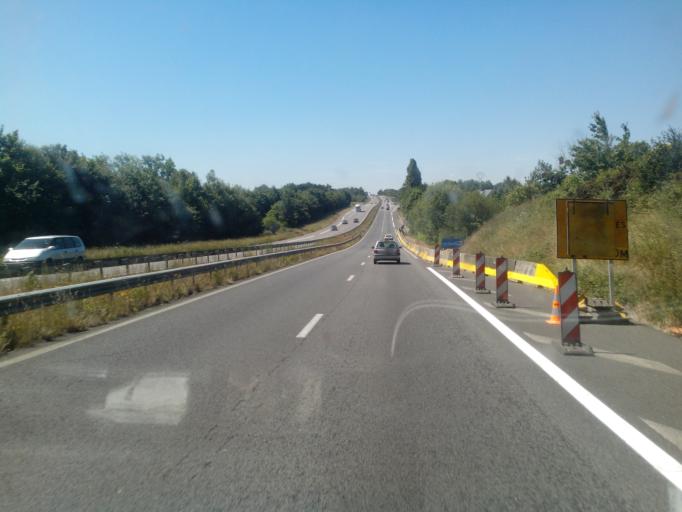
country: FR
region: Brittany
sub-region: Departement d'Ille-et-Vilaine
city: Pace
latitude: 48.1472
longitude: -1.7882
